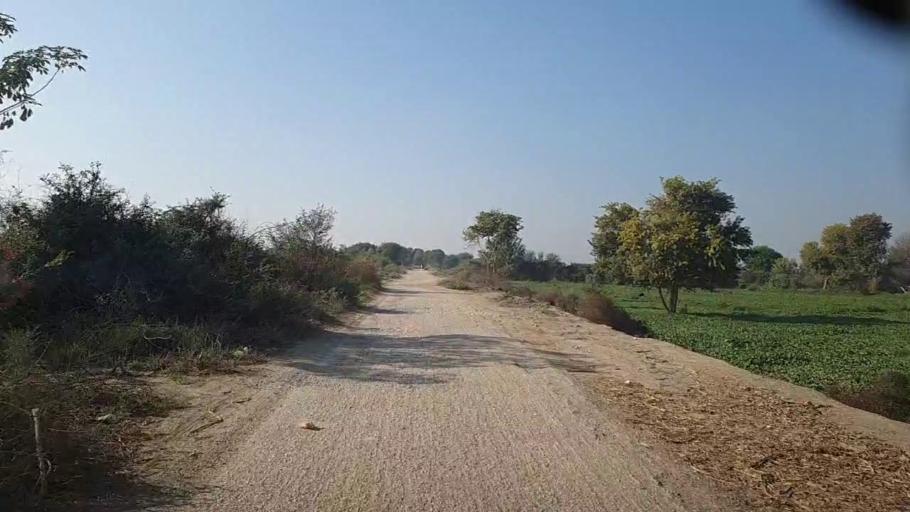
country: PK
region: Sindh
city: Darya Khan Marri
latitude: 26.6774
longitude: 68.3739
